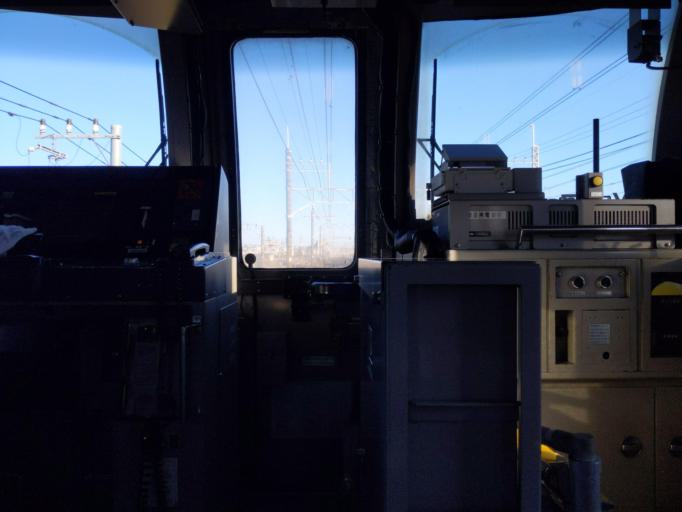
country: JP
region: Chiba
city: Funabashi
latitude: 35.7132
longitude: 139.9461
